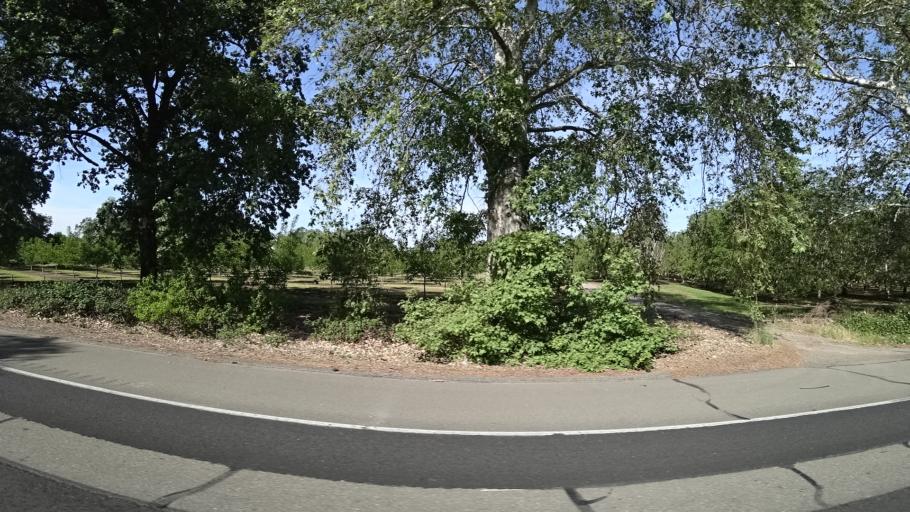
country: US
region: California
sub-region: Tehama County
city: Los Molinos
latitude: 39.9387
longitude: -122.0443
